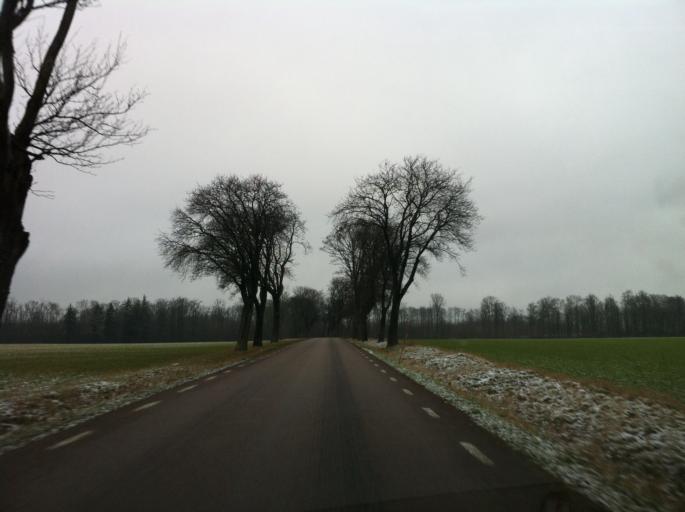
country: SE
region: Skane
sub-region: Landskrona
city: Asmundtorp
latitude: 55.9268
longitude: 12.9991
